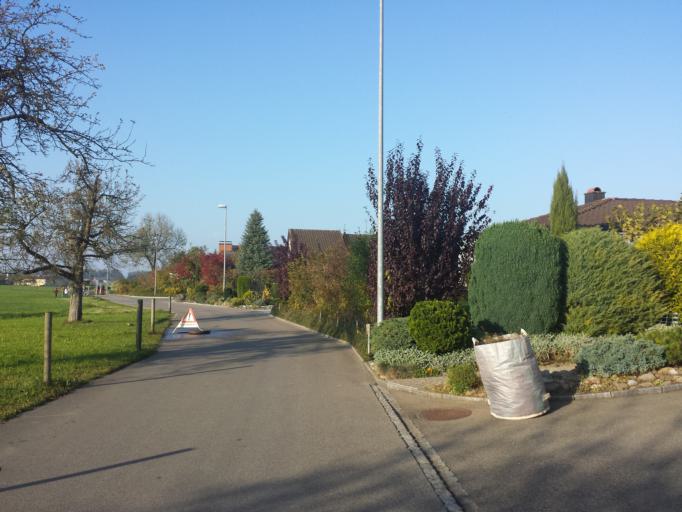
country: CH
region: Thurgau
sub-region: Arbon District
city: Salmsach
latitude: 47.5674
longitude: 9.3597
